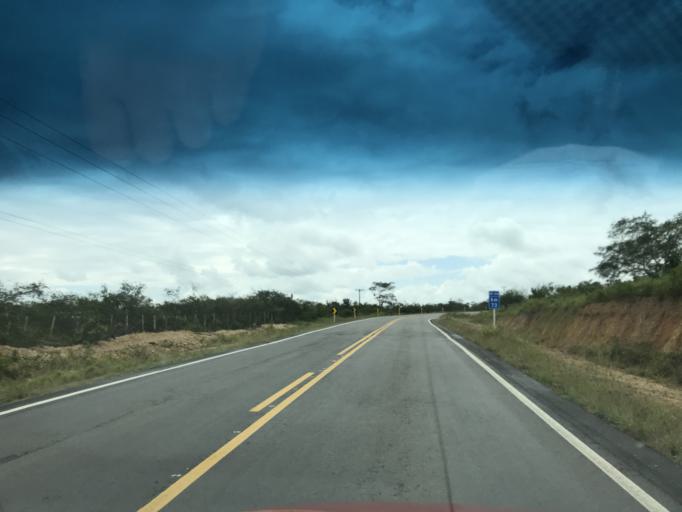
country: BR
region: Bahia
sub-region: Conceicao Do Almeida
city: Conceicao do Almeida
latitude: -12.6672
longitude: -39.2848
